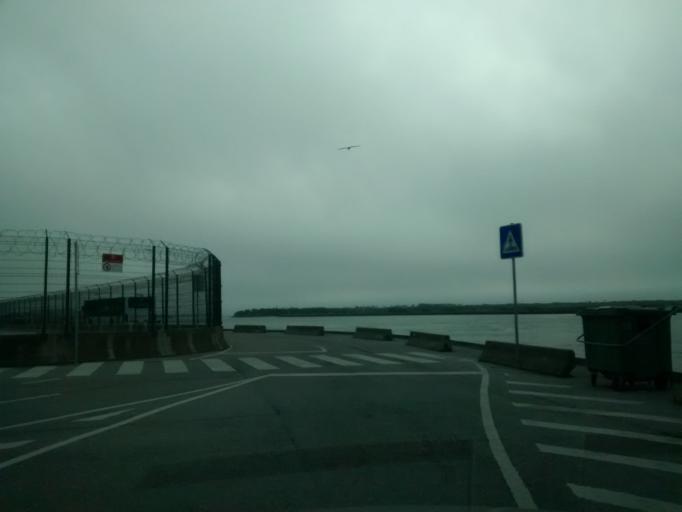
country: PT
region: Aveiro
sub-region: Ilhavo
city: Gafanha da Nazare
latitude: 40.6503
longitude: -8.7309
